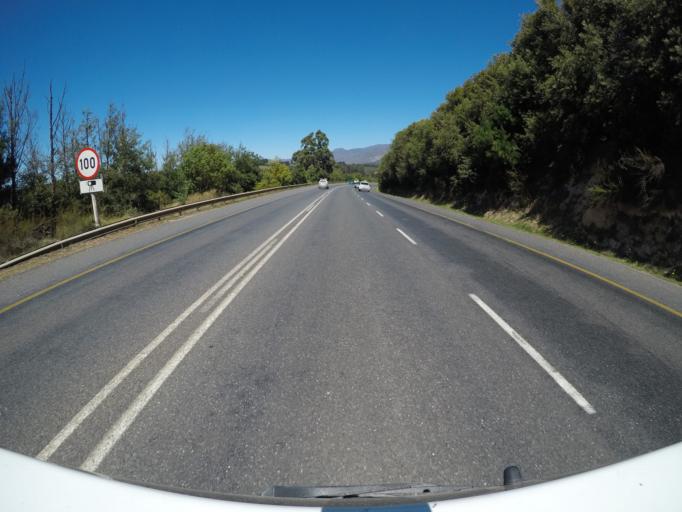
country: ZA
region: Western Cape
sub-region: Overberg District Municipality
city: Grabouw
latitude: -34.1639
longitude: 19.0272
